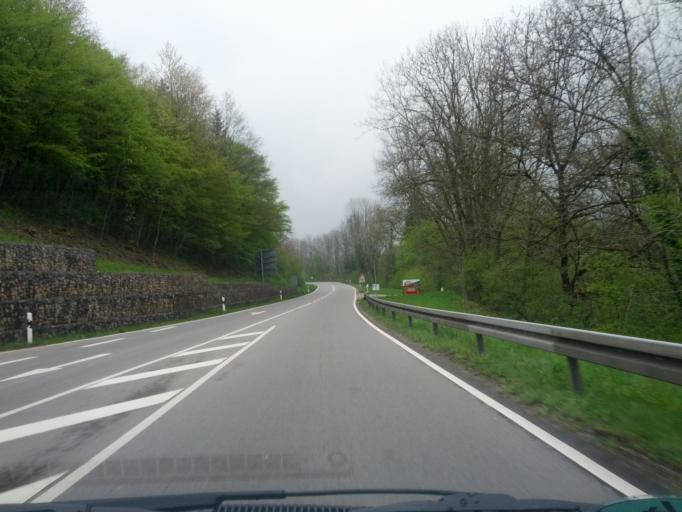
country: DE
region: Baden-Wuerttemberg
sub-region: Freiburg Region
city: Wehr
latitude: 47.6367
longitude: 7.8951
